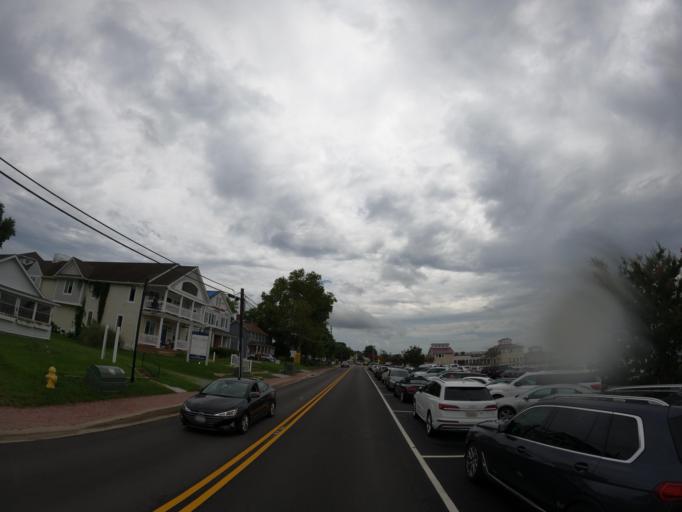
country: US
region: Maryland
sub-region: Calvert County
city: Solomons
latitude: 38.3219
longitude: -76.4594
